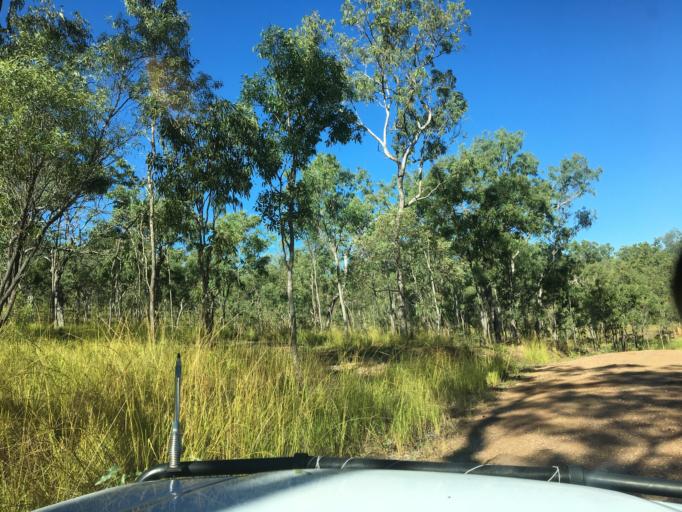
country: AU
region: Queensland
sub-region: Tablelands
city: Mareeba
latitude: -16.9652
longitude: 145.2462
